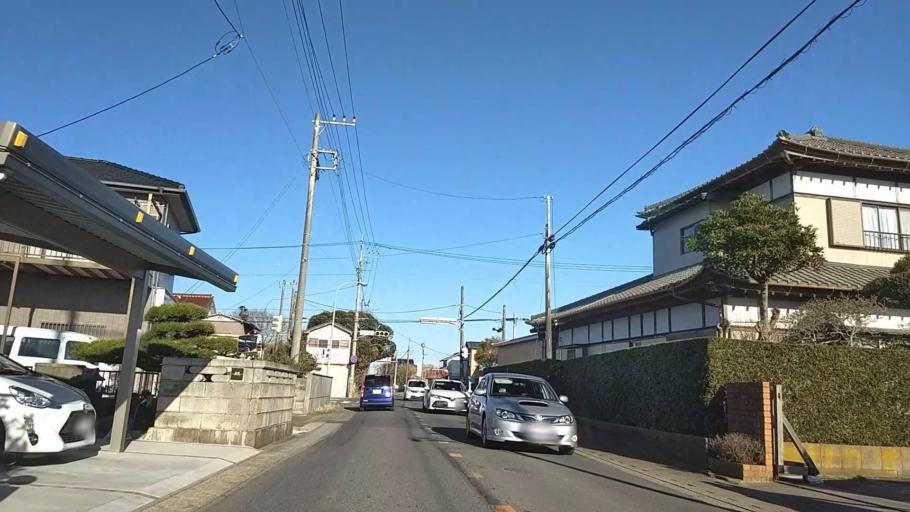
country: JP
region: Chiba
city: Yokaichiba
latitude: 35.6193
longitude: 140.5382
